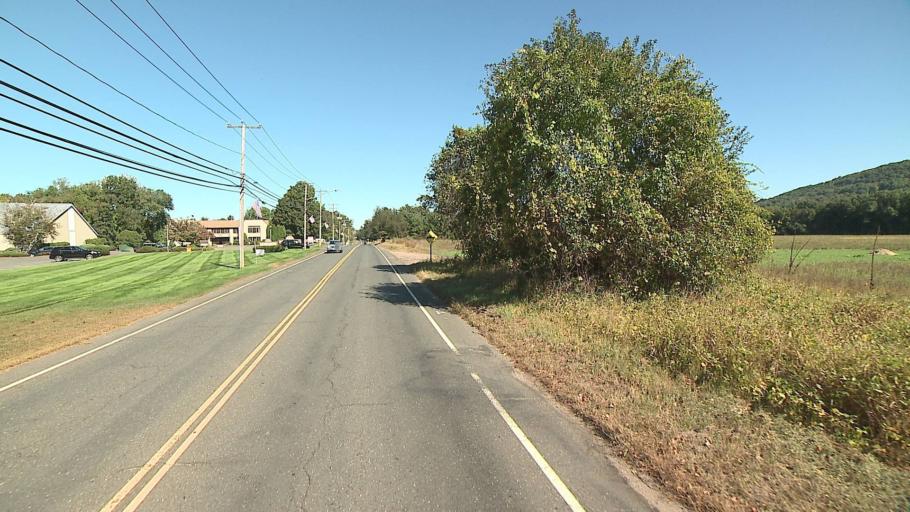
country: US
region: Connecticut
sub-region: Hartford County
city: Weatogue
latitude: 41.8393
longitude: -72.8155
